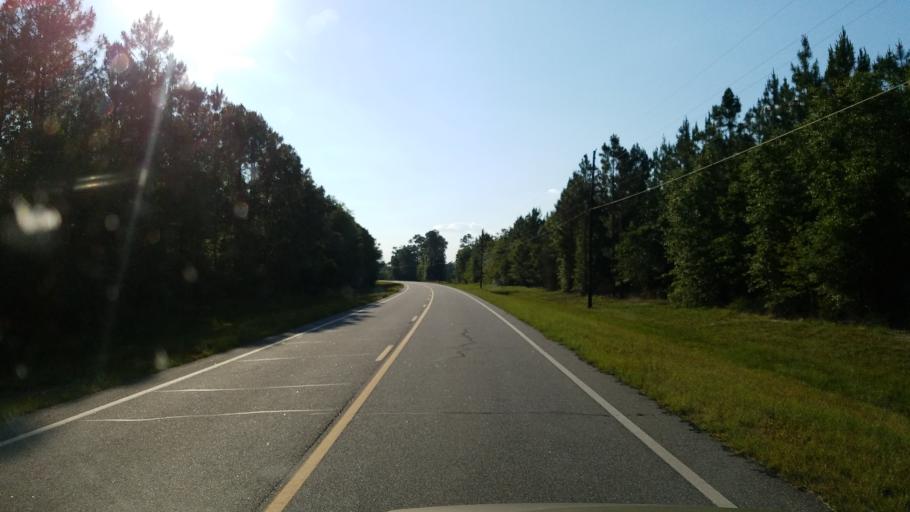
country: US
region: Georgia
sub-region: Lanier County
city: Lakeland
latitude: 30.9018
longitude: -83.0680
